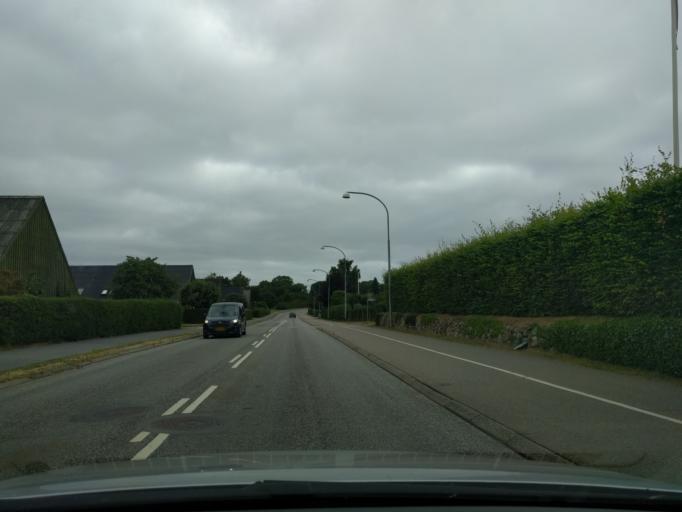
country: DK
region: Capital Region
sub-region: Helsingor Kommune
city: Espergaerde
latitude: 56.0021
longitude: 12.5388
